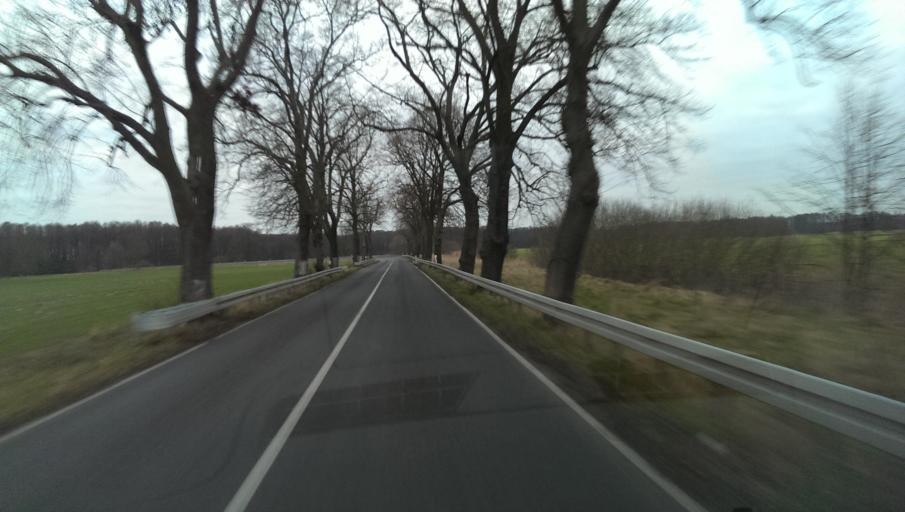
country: DE
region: Brandenburg
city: Am Mellensee
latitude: 52.1603
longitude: 13.4262
